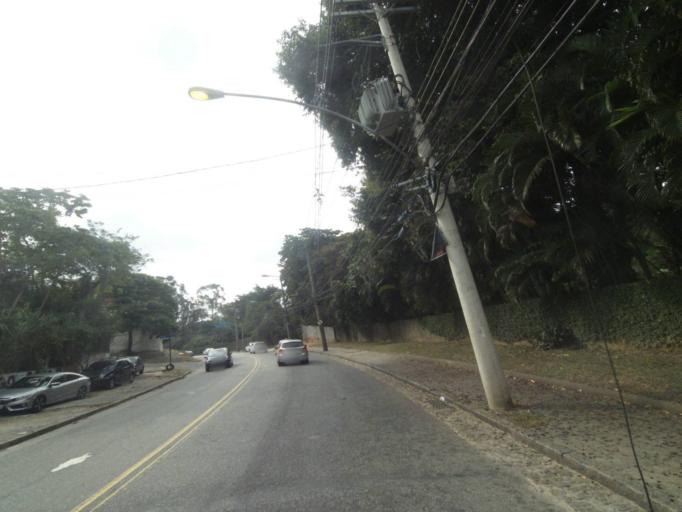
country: BR
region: Rio de Janeiro
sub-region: Sao Joao De Meriti
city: Sao Joao de Meriti
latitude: -22.9084
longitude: -43.3785
